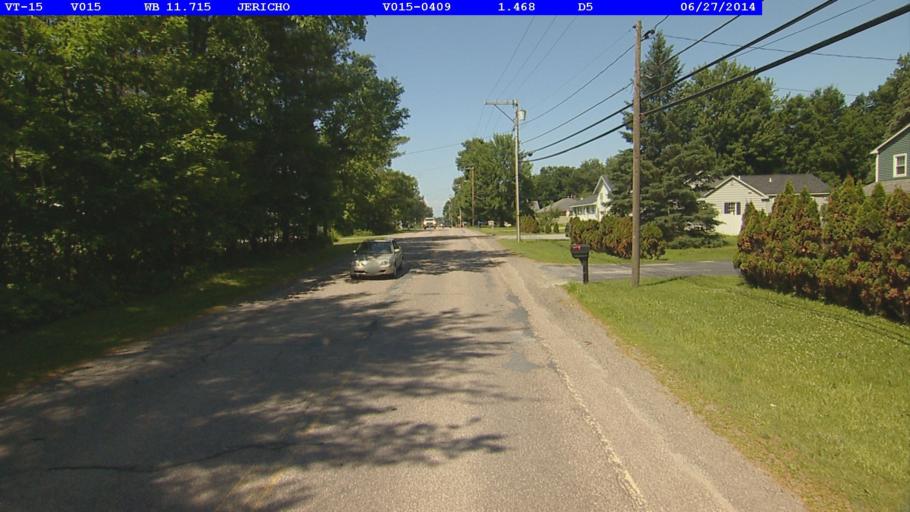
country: US
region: Vermont
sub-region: Chittenden County
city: Jericho
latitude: 44.5095
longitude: -72.9794
